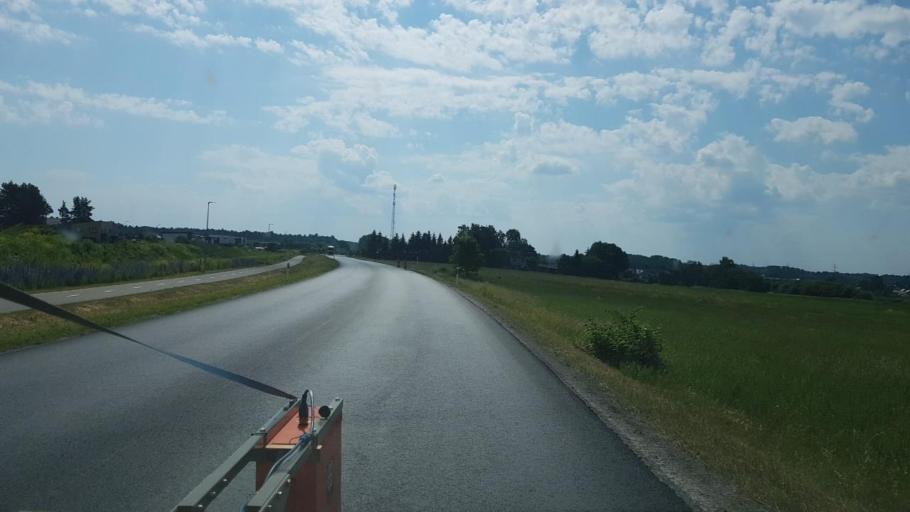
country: EE
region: Harju
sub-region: Saue vald
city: Laagri
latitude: 59.3693
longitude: 24.5858
